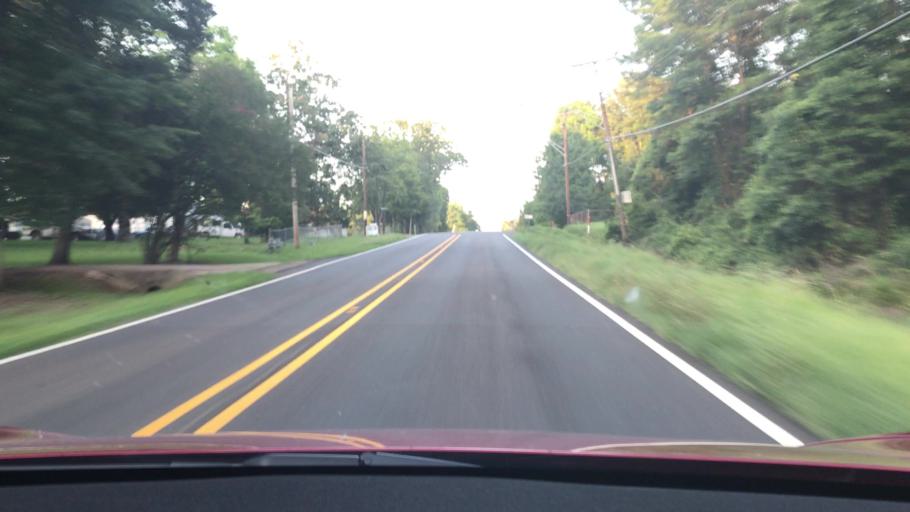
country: US
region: Louisiana
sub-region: De Soto Parish
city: Stonewall
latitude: 32.3910
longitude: -93.7608
